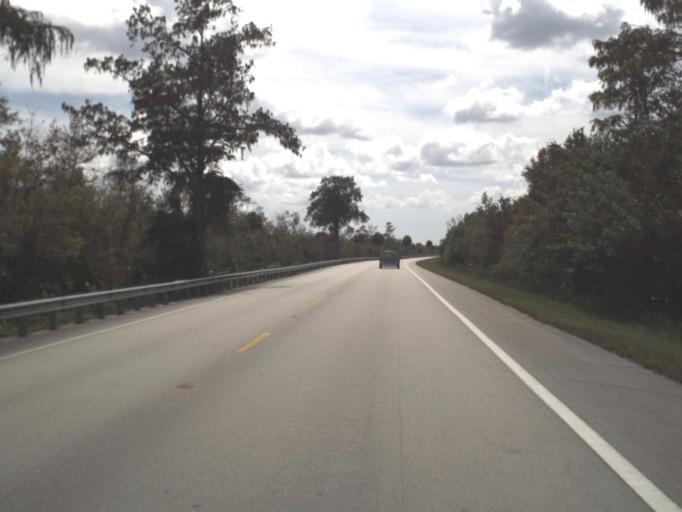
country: US
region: Florida
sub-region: Collier County
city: Lely Resort
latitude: 25.9375
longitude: -81.3572
